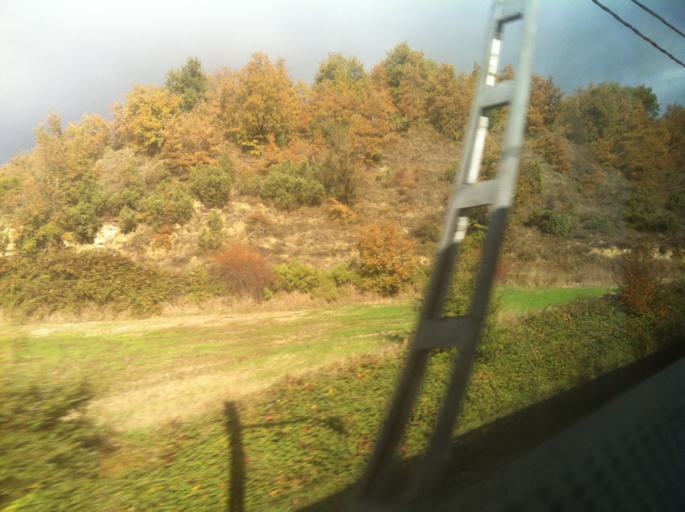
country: ES
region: Basque Country
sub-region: Provincia de Alava
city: Arminon
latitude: 42.7385
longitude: -2.8737
